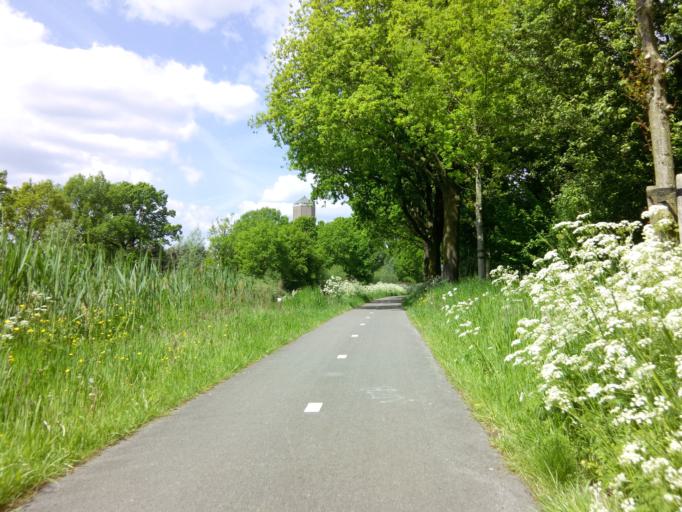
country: NL
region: Utrecht
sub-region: Gemeente Woudenberg
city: Woudenberg
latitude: 52.0795
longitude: 5.4608
